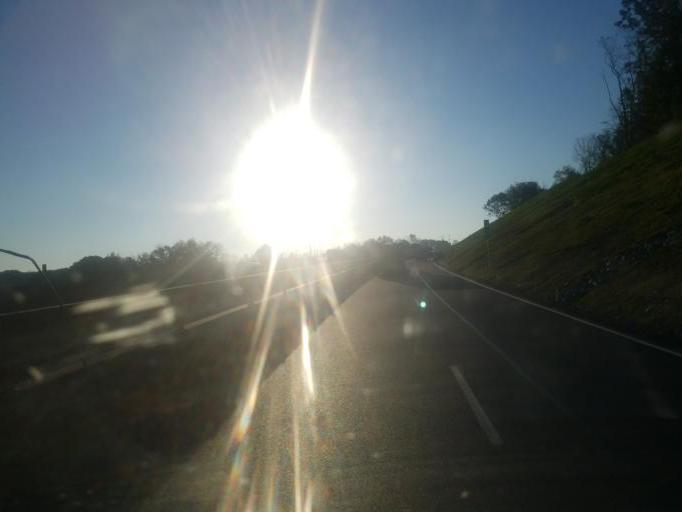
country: US
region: Pennsylvania
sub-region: Allegheny County
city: Russellton
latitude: 40.5863
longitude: -79.8771
